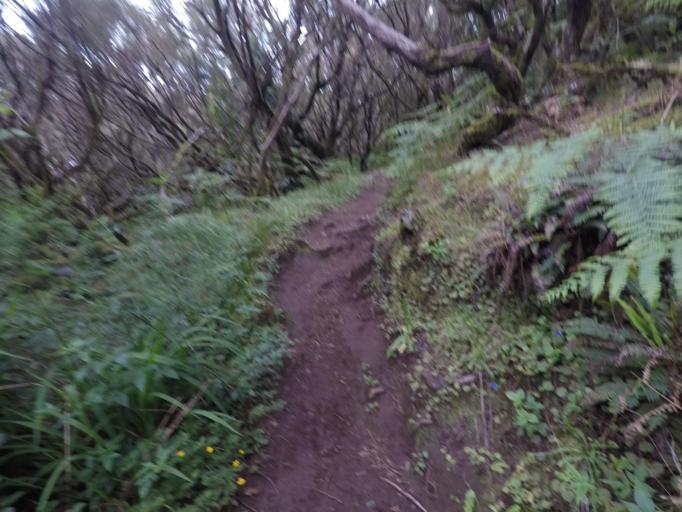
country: PT
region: Madeira
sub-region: Sao Vicente
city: Sao Vicente
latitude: 32.7718
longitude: -17.0622
